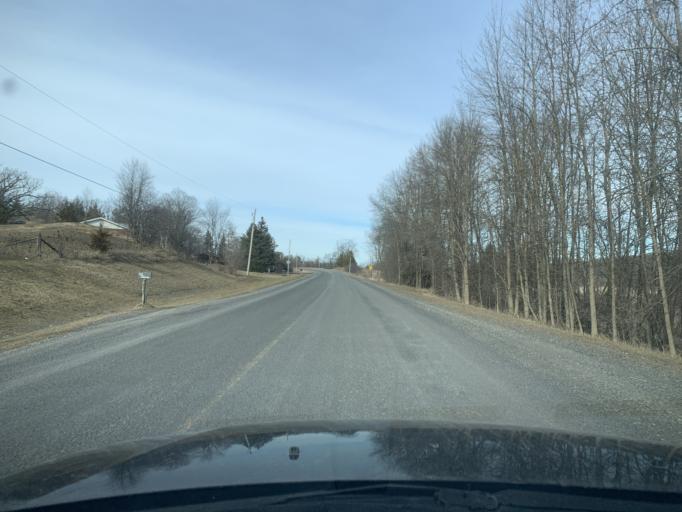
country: CA
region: Ontario
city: Greater Napanee
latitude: 44.4429
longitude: -77.0700
